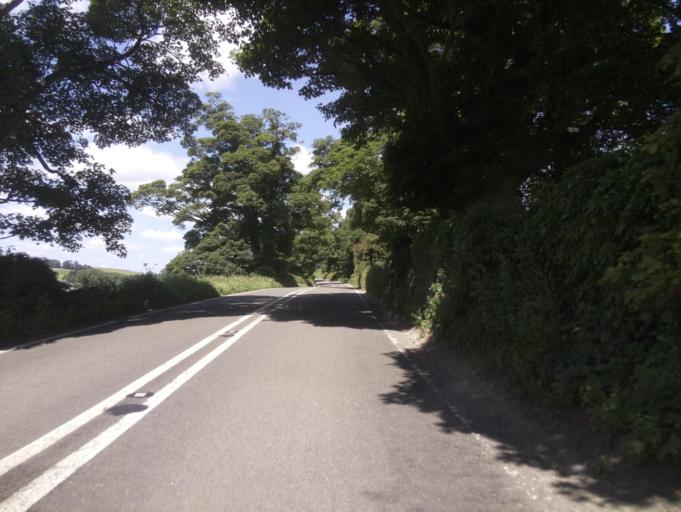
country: GB
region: England
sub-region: Derbyshire
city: Ashbourne
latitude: 53.0655
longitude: -1.7476
